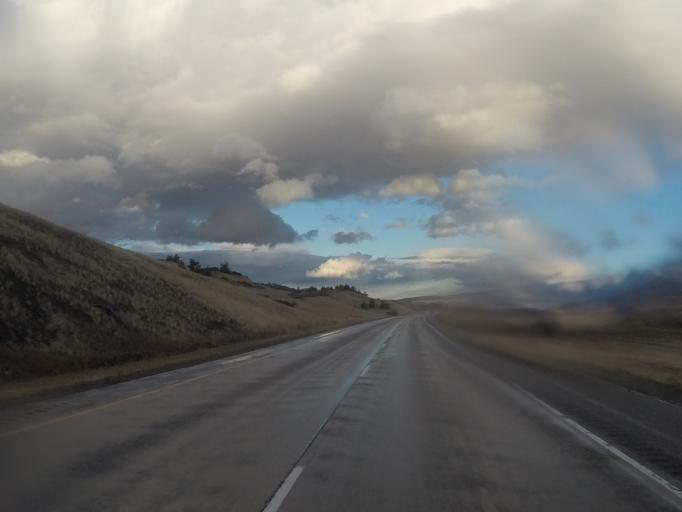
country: US
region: Montana
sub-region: Park County
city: Livingston
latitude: 45.6599
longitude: -110.6625
